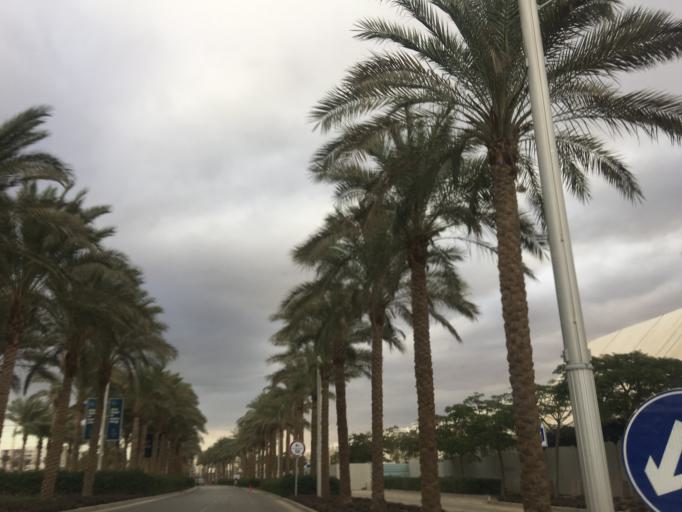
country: EG
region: Muhafazat al Qahirah
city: Cairo
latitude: 30.0304
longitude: 31.4109
